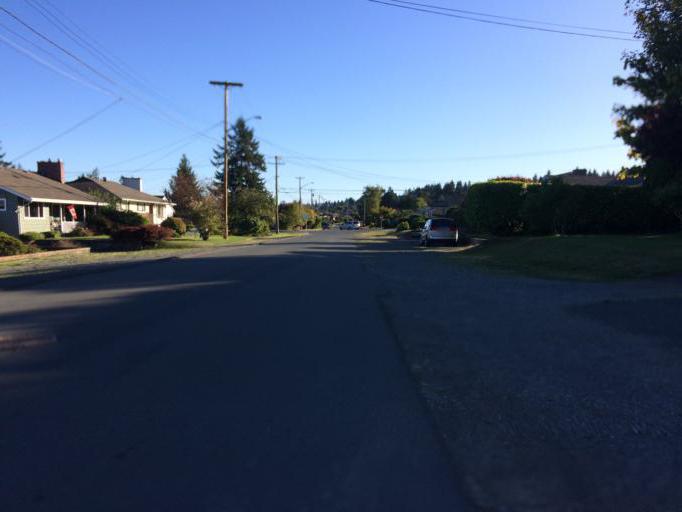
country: CA
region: British Columbia
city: Campbell River
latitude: 50.0120
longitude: -125.2366
